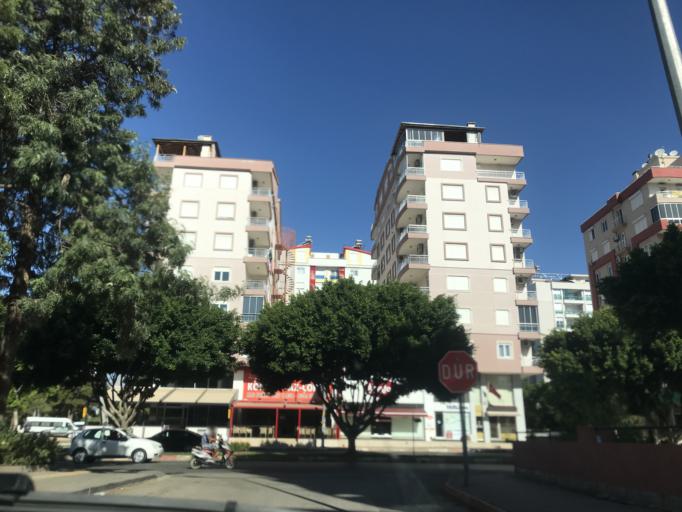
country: TR
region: Antalya
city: Antalya
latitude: 36.8956
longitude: 30.6291
